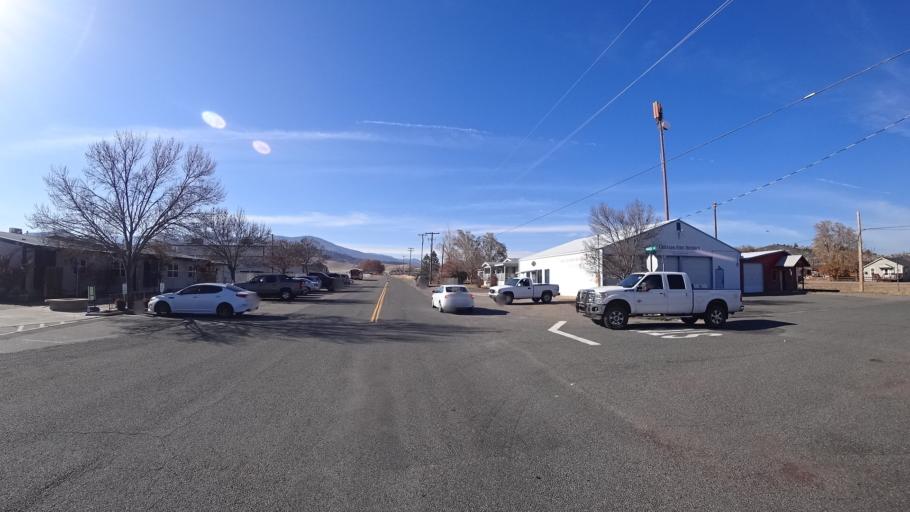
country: US
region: California
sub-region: Siskiyou County
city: Montague
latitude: 41.6456
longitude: -122.5249
